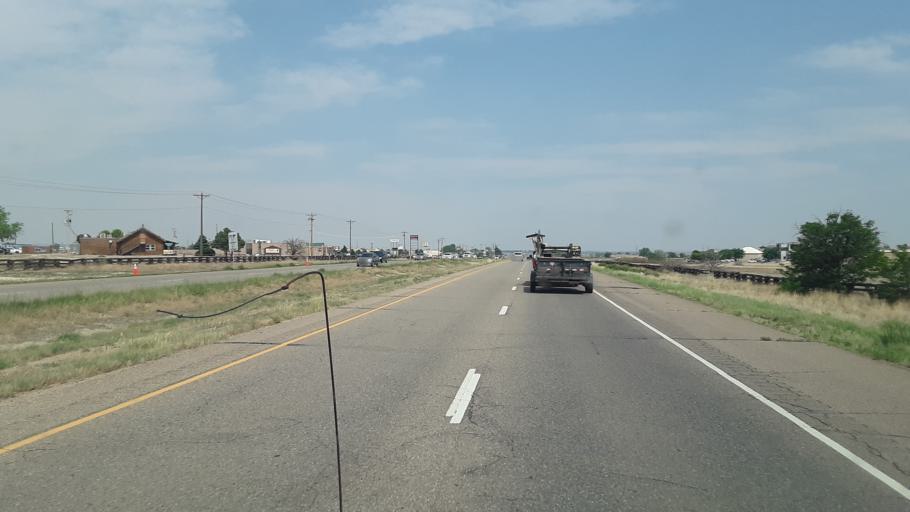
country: US
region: Colorado
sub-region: Pueblo County
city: Pueblo West
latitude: 38.3260
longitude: -104.7092
